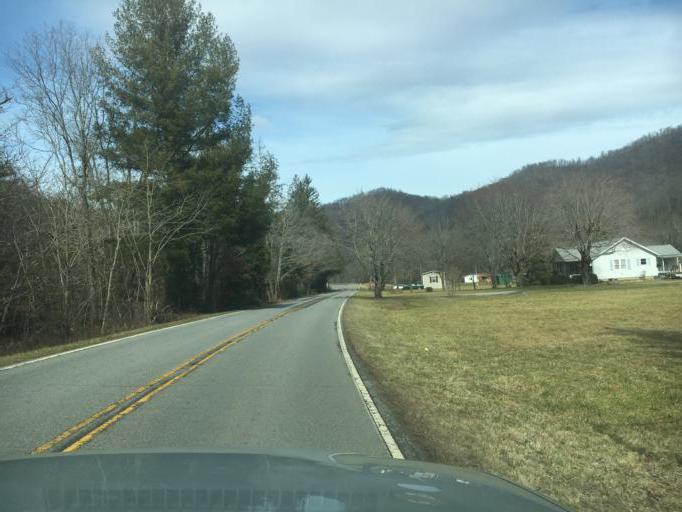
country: US
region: North Carolina
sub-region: Haywood County
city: Canton
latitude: 35.4535
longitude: -82.8412
